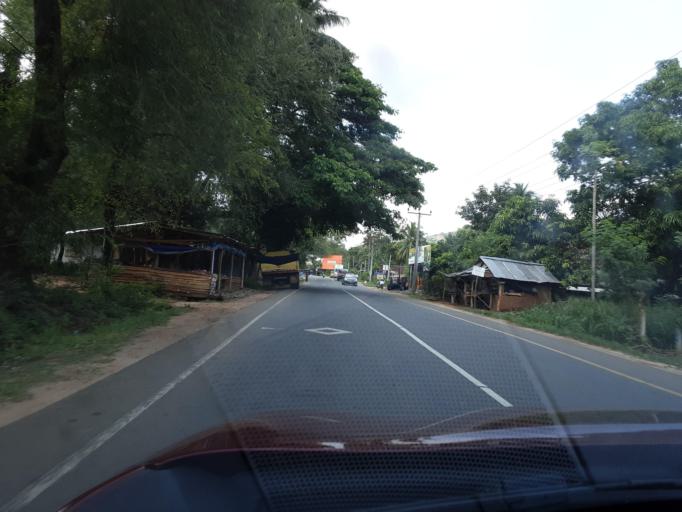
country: LK
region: Uva
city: Haputale
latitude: 6.6947
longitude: 81.1097
